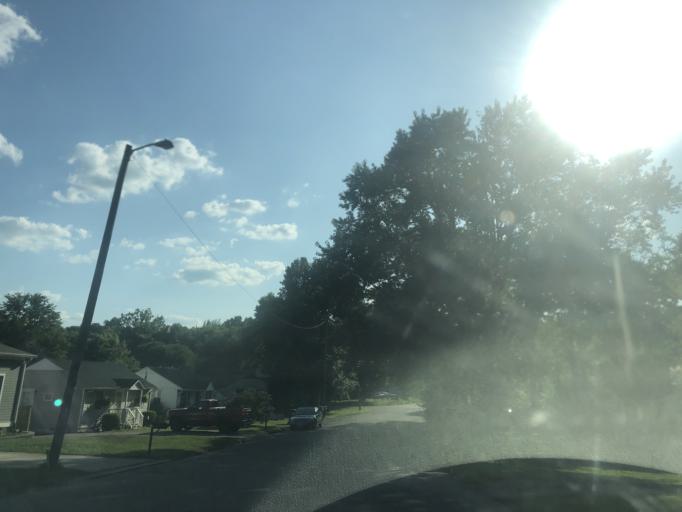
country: US
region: Tennessee
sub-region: Davidson County
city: Nashville
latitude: 36.1681
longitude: -86.7450
